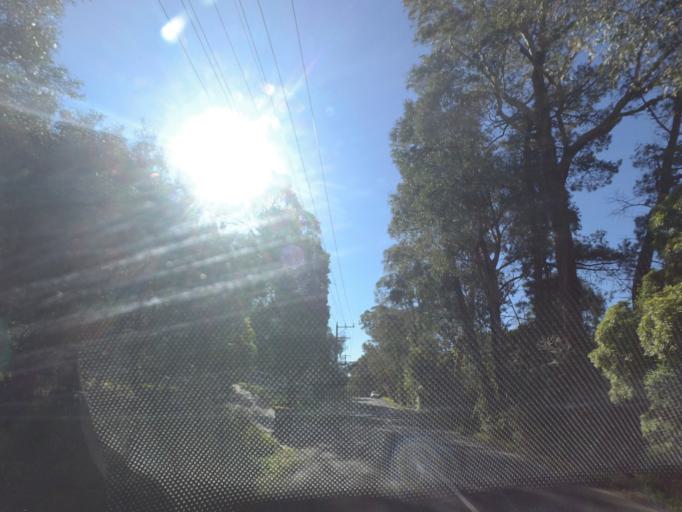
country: AU
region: Victoria
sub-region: Maroondah
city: Croydon Hills
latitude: -37.7512
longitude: 145.2714
